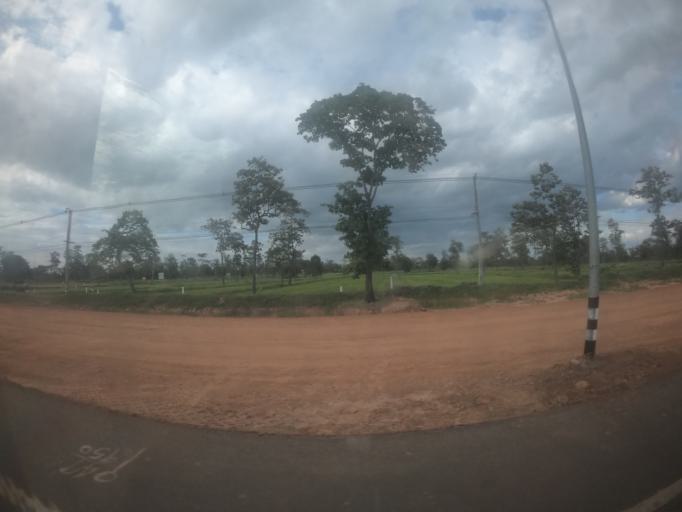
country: TH
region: Surin
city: Kap Choeng
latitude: 14.5137
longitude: 103.5493
